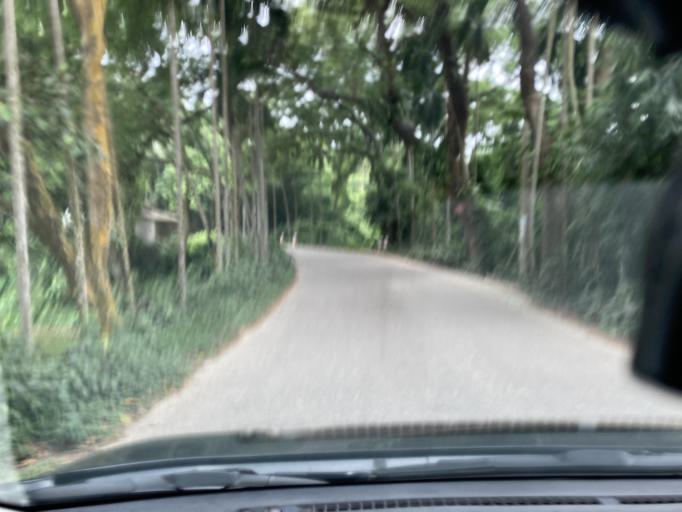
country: BD
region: Dhaka
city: Dohar
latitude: 23.7965
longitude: 90.0488
